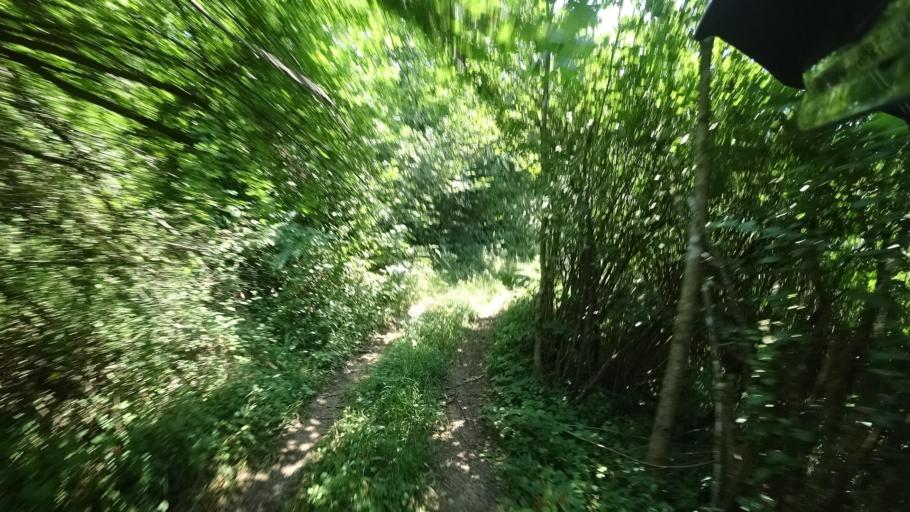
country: HR
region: Karlovacka
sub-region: Grad Ogulin
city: Ogulin
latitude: 45.3117
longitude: 15.1705
